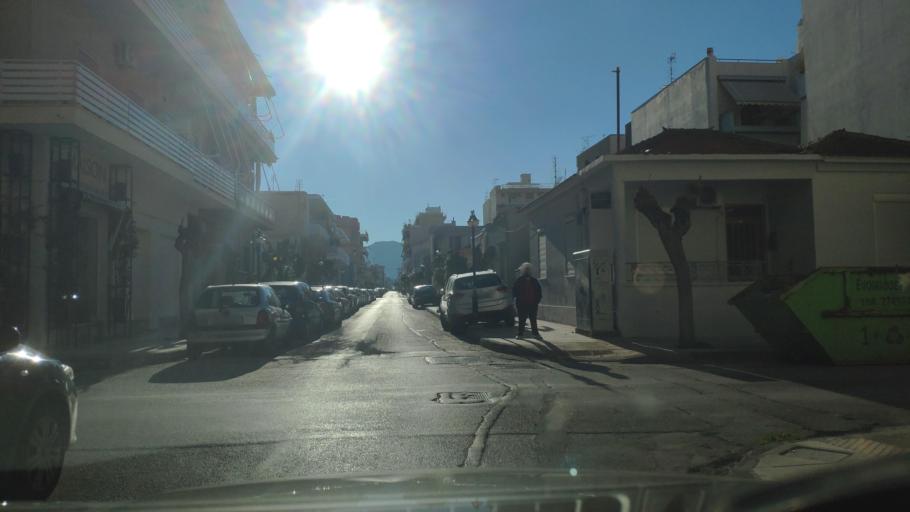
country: GR
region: Peloponnese
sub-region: Nomos Korinthias
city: Korinthos
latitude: 37.9417
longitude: 22.9292
